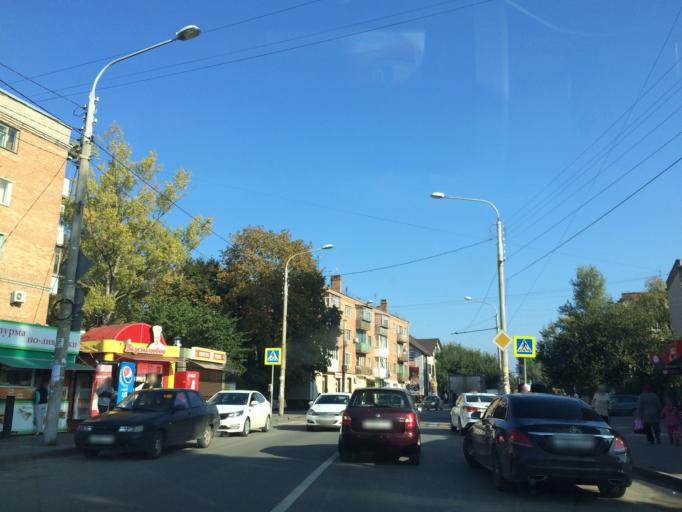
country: RU
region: Rostov
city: Imeni Chkalova
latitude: 47.2675
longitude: 39.7874
